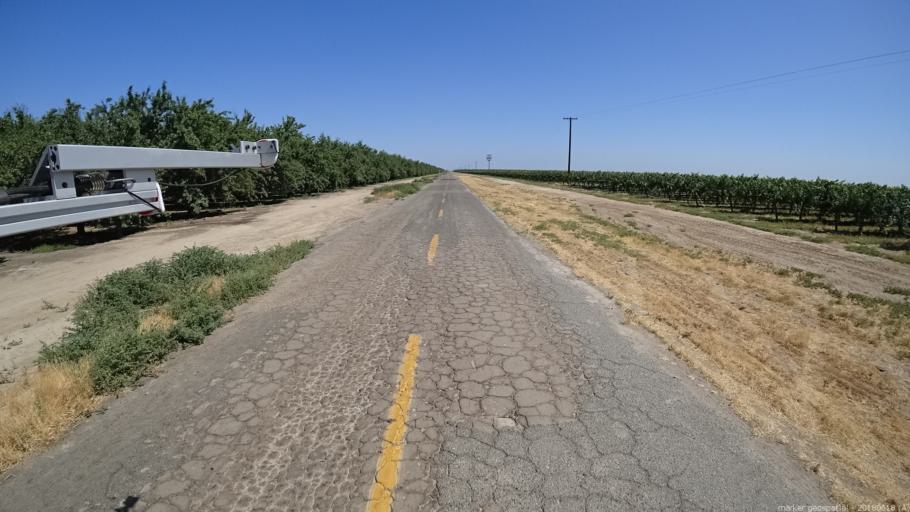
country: US
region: California
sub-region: Madera County
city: Parkwood
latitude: 36.8443
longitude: -120.1828
